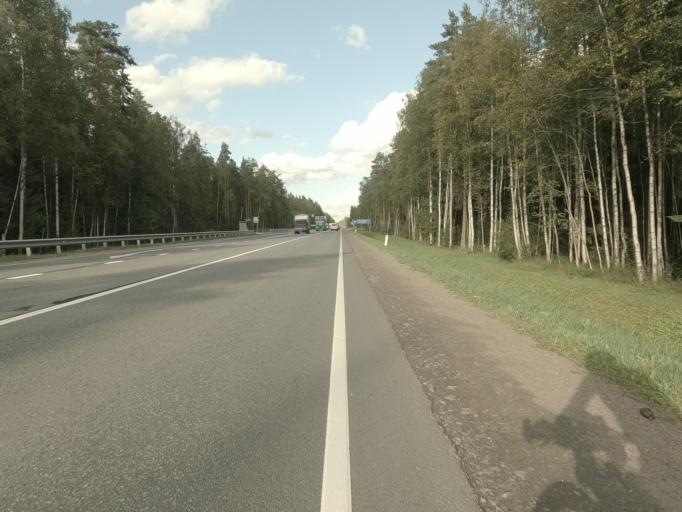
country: RU
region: Leningrad
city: Mga
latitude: 59.7061
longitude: 31.0127
